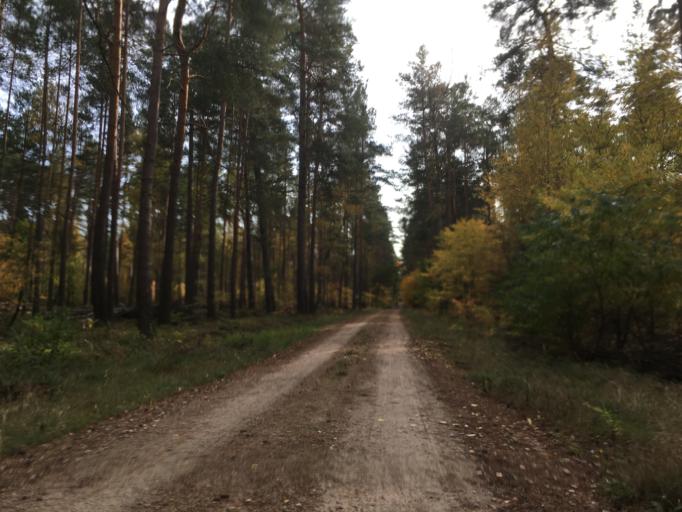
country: DE
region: Brandenburg
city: Liebenwalde
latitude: 52.9345
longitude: 13.5028
